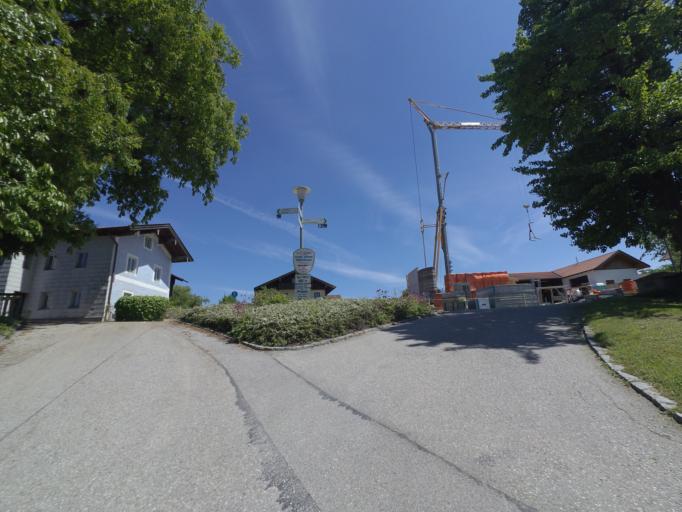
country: DE
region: Bavaria
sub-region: Upper Bavaria
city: Taching am See
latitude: 47.9549
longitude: 12.7533
